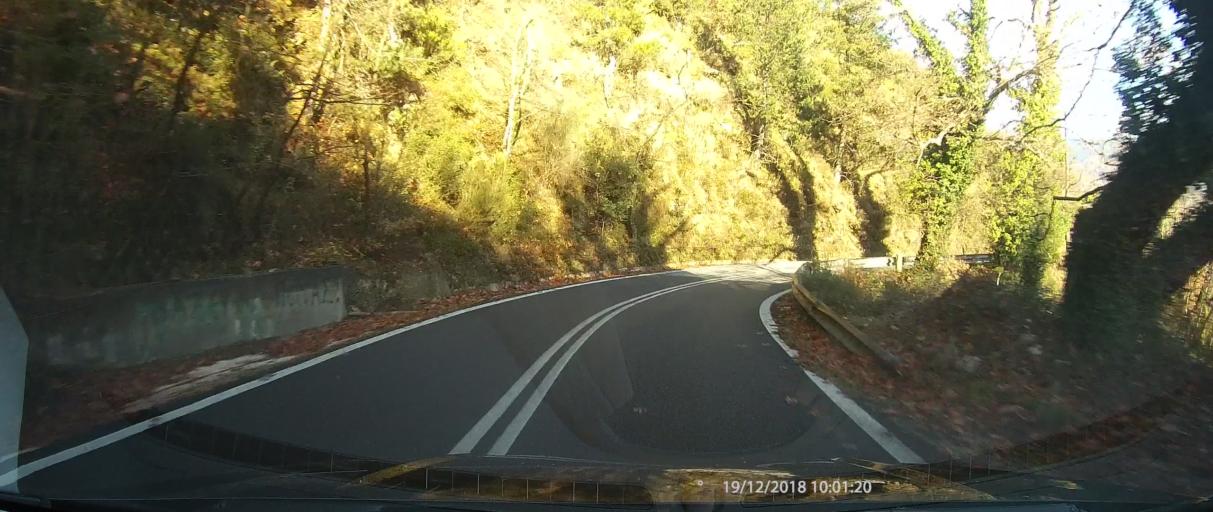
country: GR
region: Peloponnese
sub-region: Nomos Messinias
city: Paralia Vergas
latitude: 37.0942
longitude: 22.2296
